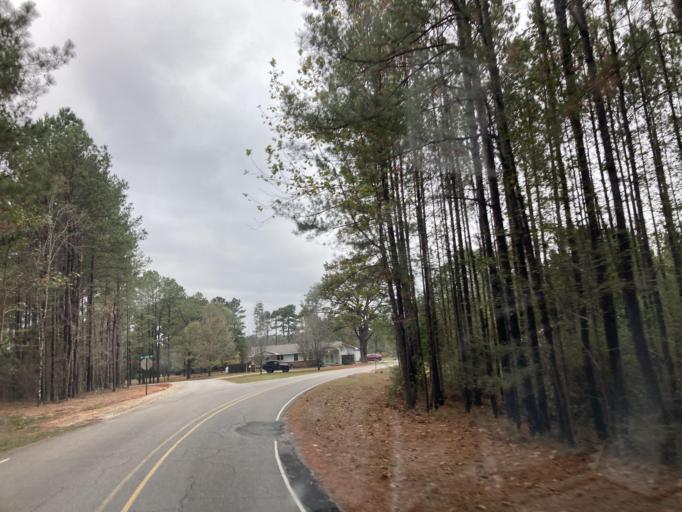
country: US
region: Mississippi
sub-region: Lamar County
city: Purvis
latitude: 31.1842
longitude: -89.4229
